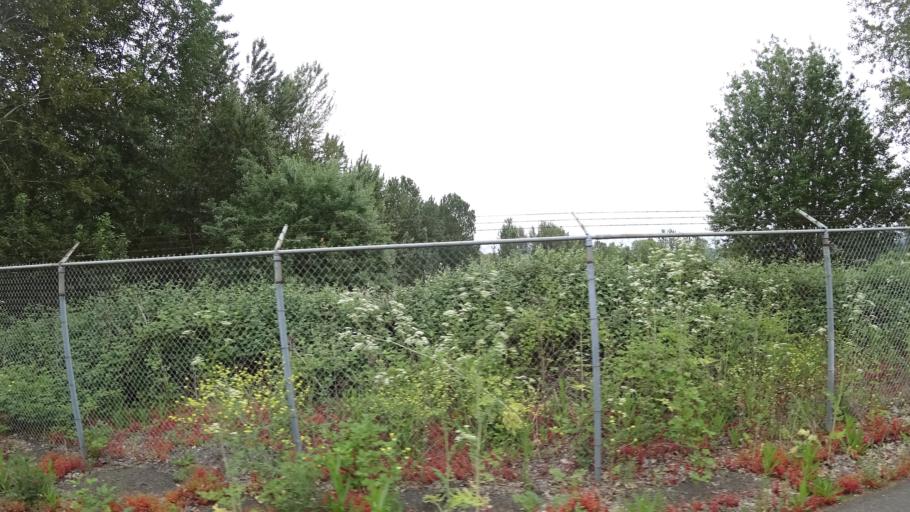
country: US
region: Washington
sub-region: Clark County
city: Vancouver
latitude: 45.6055
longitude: -122.6908
